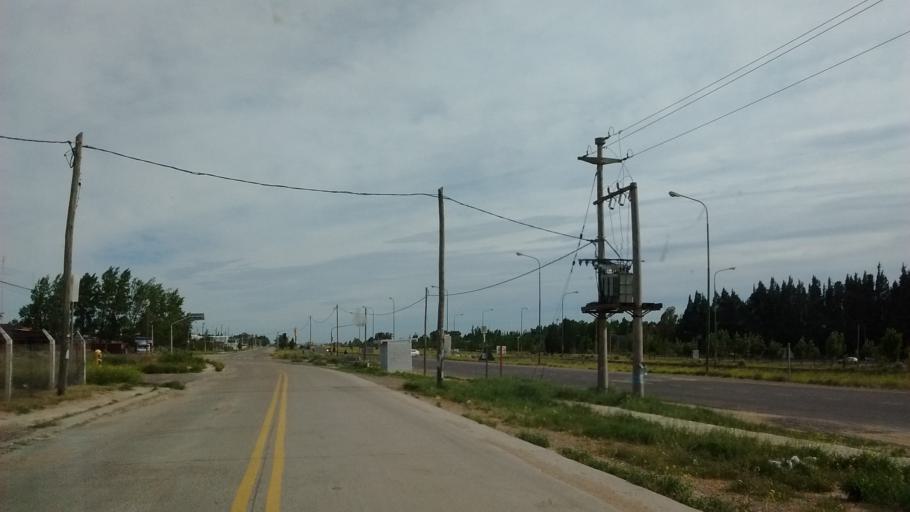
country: AR
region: Neuquen
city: Neuquen
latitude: -38.9086
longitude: -68.0826
